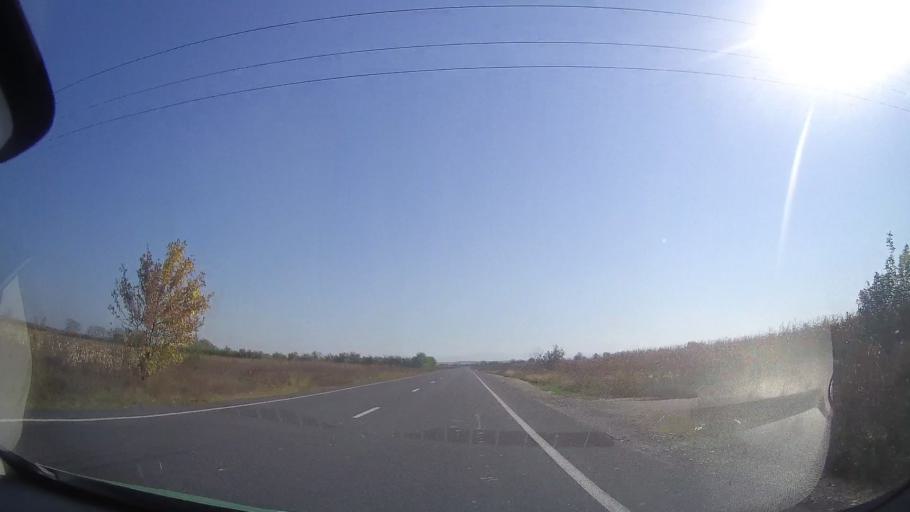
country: RO
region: Timis
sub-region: Comuna Costeiu
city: Costeiu
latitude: 45.7431
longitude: 21.8197
